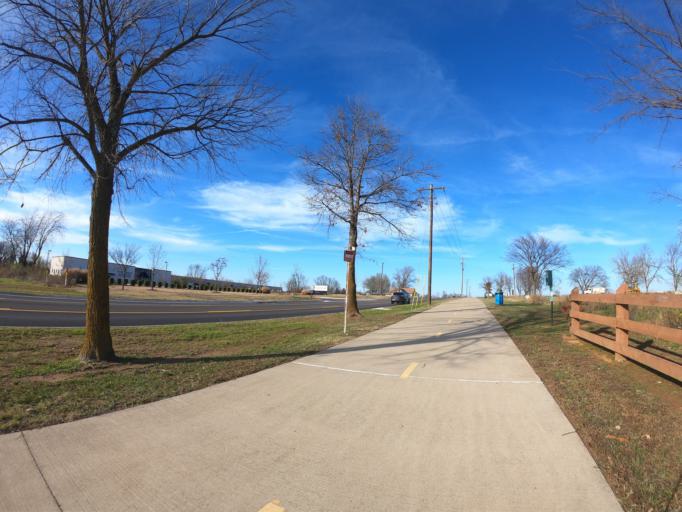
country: US
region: Arkansas
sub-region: Benton County
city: Lowell
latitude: 36.2580
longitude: -94.1547
